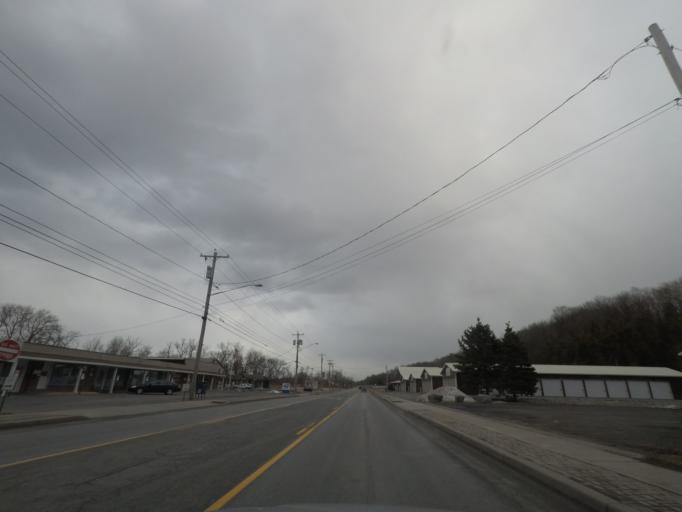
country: US
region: New York
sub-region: Madison County
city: Chittenango
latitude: 43.0541
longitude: -75.8611
